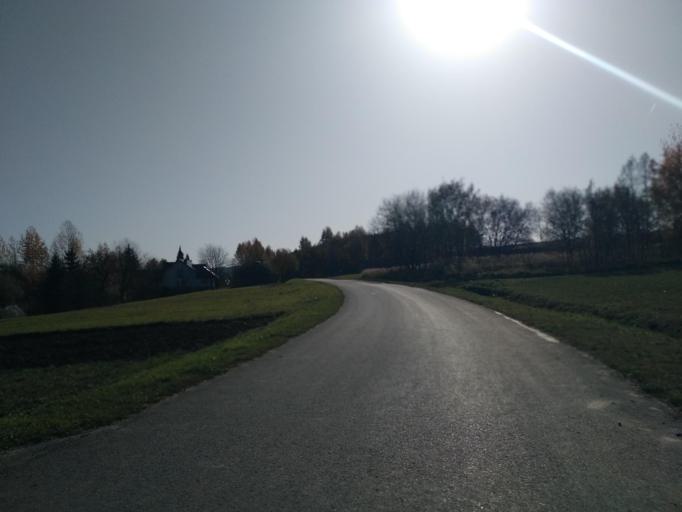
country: PL
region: Subcarpathian Voivodeship
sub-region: Powiat rzeszowski
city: Blazowa
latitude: 49.8639
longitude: 22.1237
